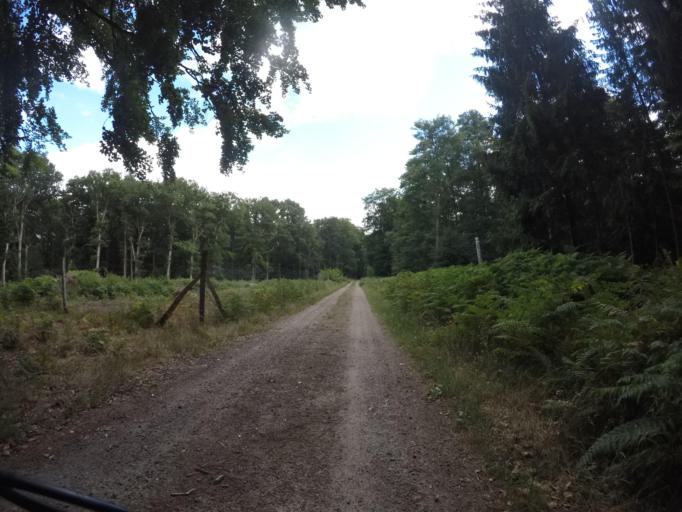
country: DE
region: Mecklenburg-Vorpommern
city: Lubtheen
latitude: 53.2808
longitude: 10.9822
